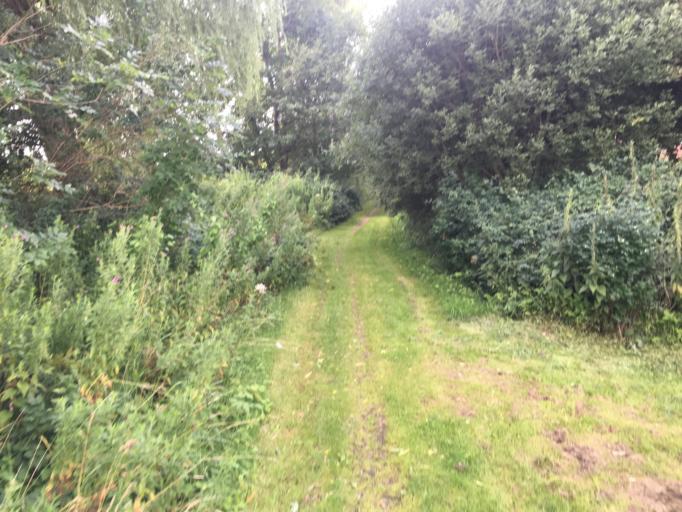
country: DK
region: Capital Region
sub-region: Fredensborg Kommune
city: Niva
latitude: 55.9314
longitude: 12.4838
